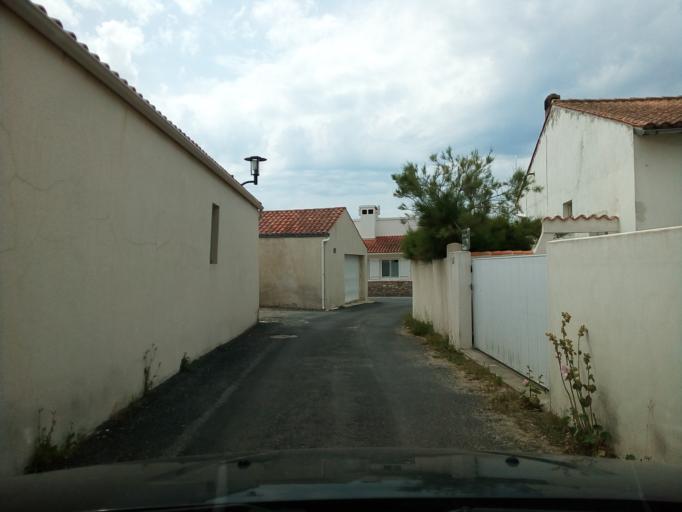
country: FR
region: Poitou-Charentes
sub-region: Departement de la Charente-Maritime
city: Dolus-d'Oleron
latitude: 45.9171
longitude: -1.3339
